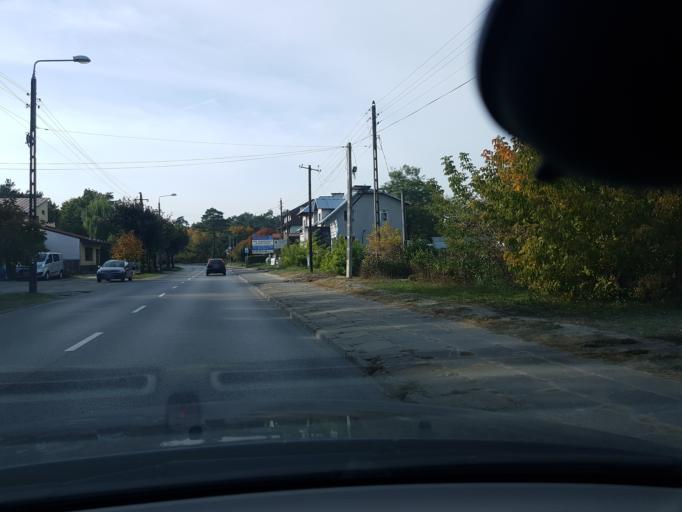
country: PL
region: Masovian Voivodeship
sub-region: Powiat otwocki
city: Otwock
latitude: 52.1068
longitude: 21.2556
